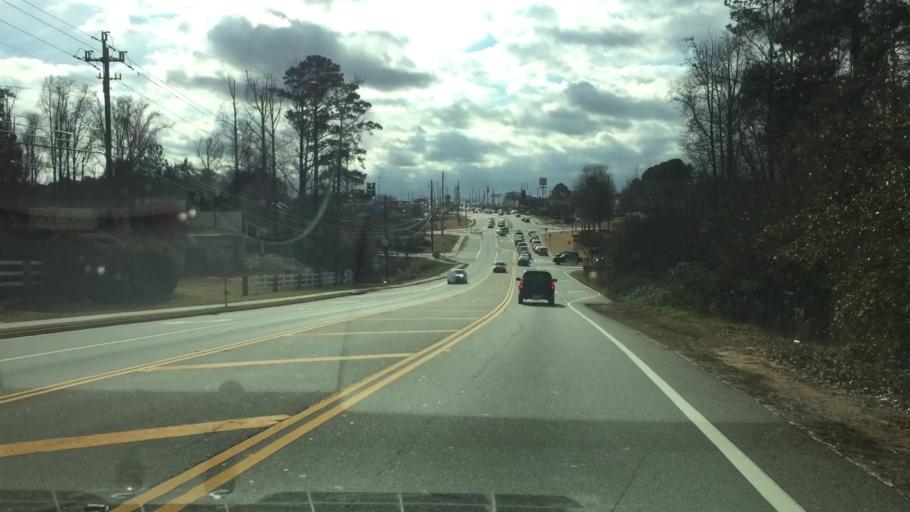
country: US
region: Georgia
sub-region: Henry County
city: McDonough
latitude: 33.4331
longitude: -84.1759
